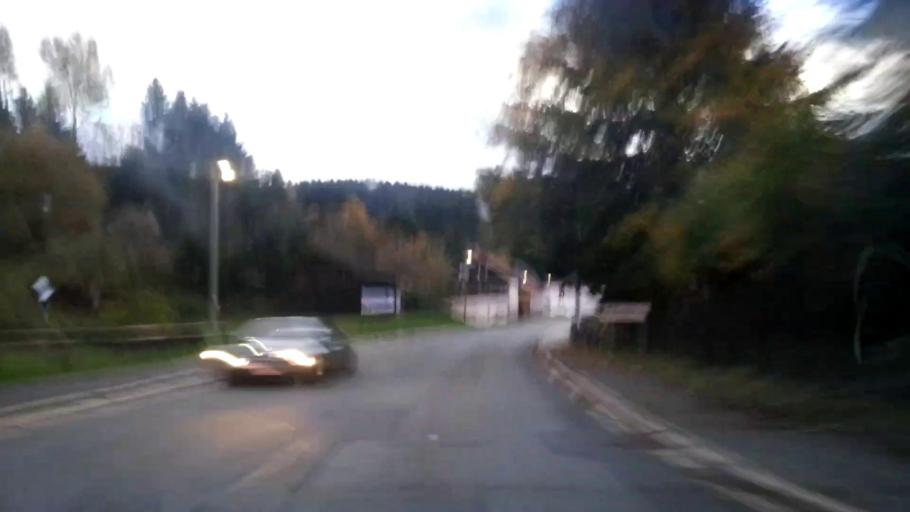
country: DE
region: Bavaria
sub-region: Upper Franconia
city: Warmensteinach
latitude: 50.0015
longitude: 11.8031
